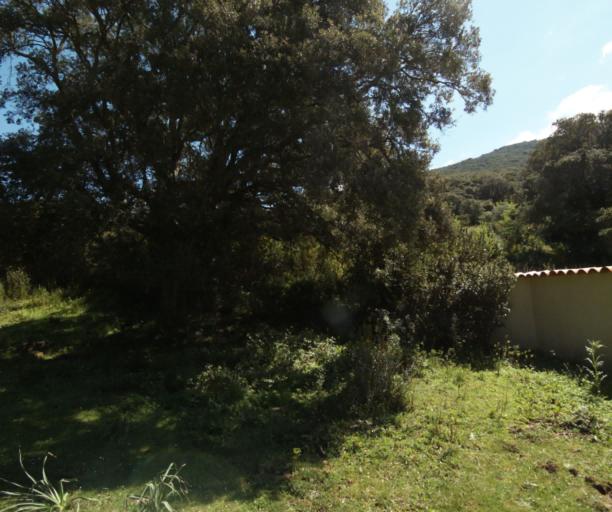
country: FR
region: Corsica
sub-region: Departement de la Corse-du-Sud
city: Propriano
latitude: 41.6393
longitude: 8.8691
